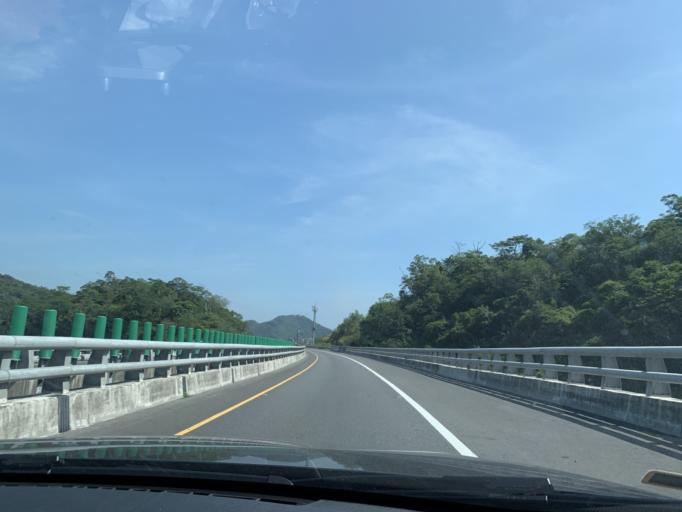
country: TW
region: Taiwan
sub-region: Yilan
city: Yilan
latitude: 24.5690
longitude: 121.8475
